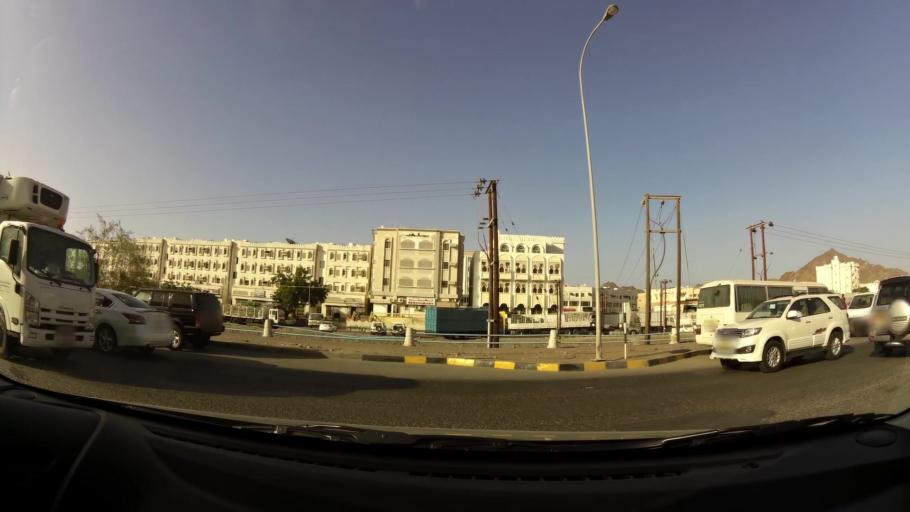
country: OM
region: Muhafazat Masqat
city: Muscat
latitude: 23.5864
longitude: 58.5541
